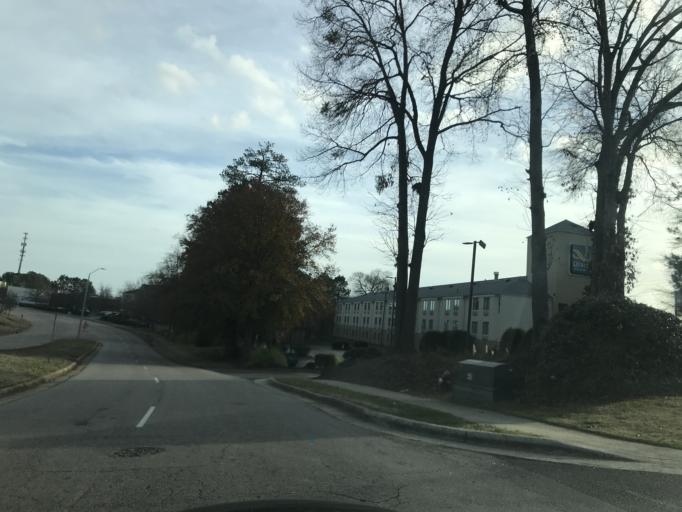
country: US
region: North Carolina
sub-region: Wake County
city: Raleigh
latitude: 35.8129
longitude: -78.6021
